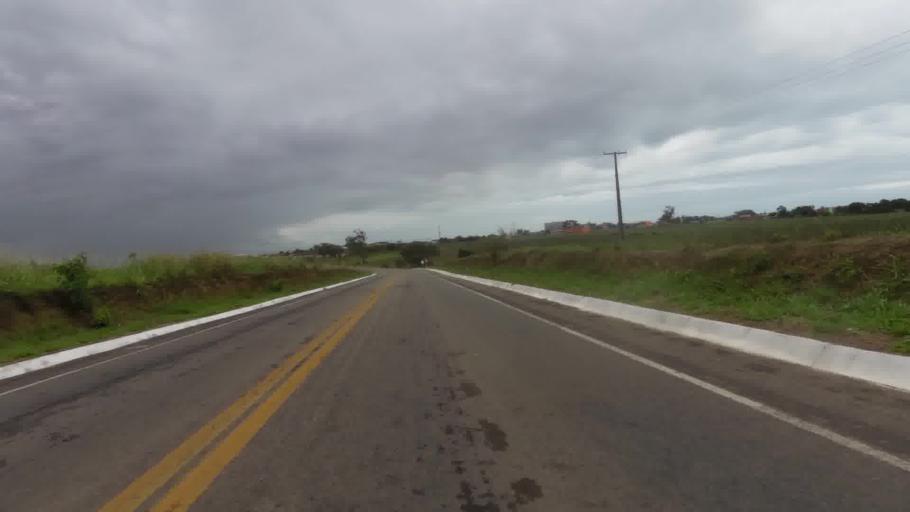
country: BR
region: Espirito Santo
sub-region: Marataizes
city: Marataizes
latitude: -21.0507
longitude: -40.8461
